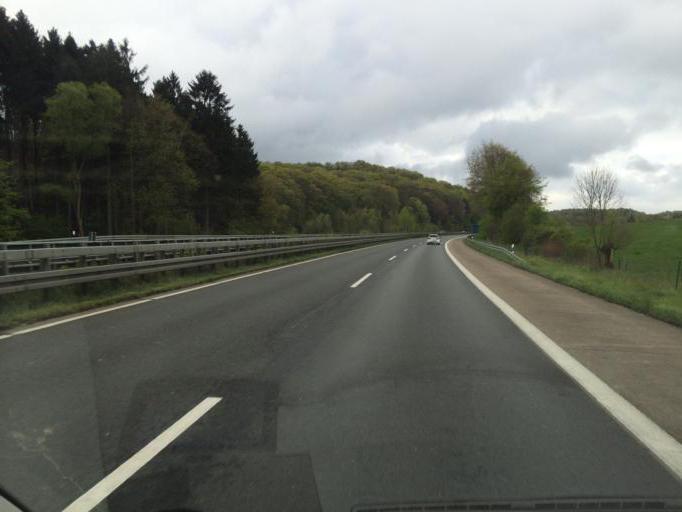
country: DE
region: North Rhine-Westphalia
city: Sprockhovel
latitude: 51.3492
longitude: 7.2749
